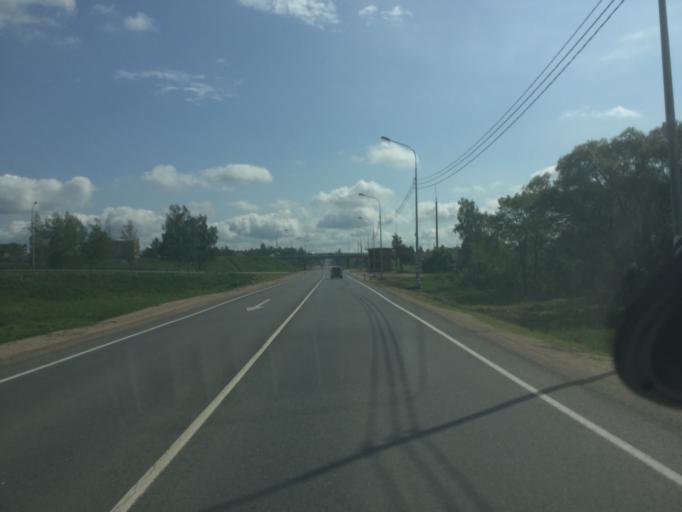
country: RU
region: Smolensk
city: Katyn'
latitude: 54.7775
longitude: 31.7957
